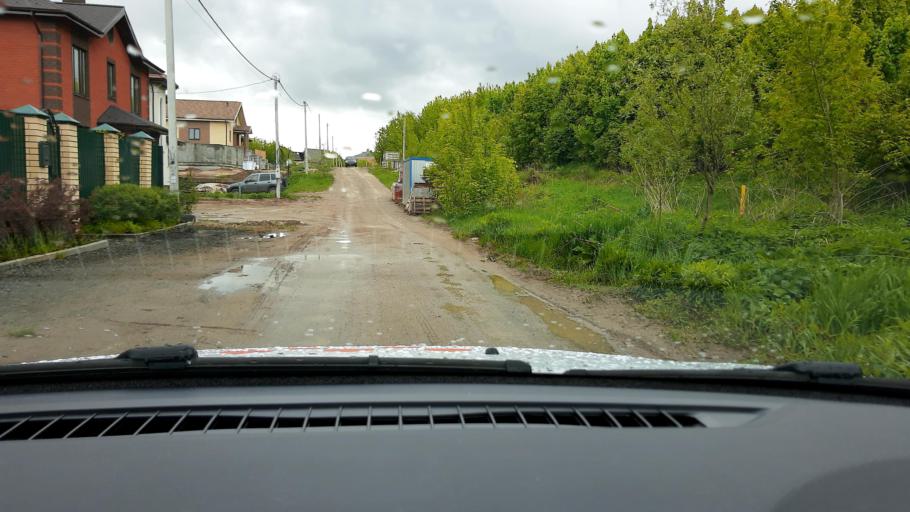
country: RU
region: Nizjnij Novgorod
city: Afonino
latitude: 56.2711
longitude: 44.0987
